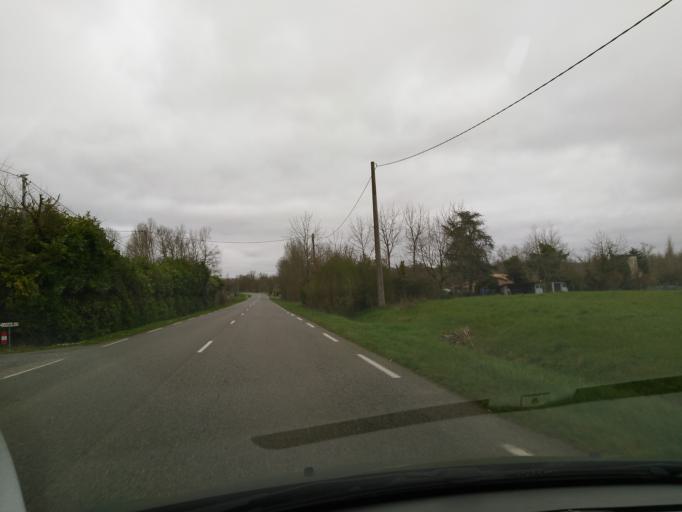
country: FR
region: Aquitaine
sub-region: Departement du Lot-et-Garonne
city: Castillonnes
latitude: 44.6679
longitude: 0.5828
